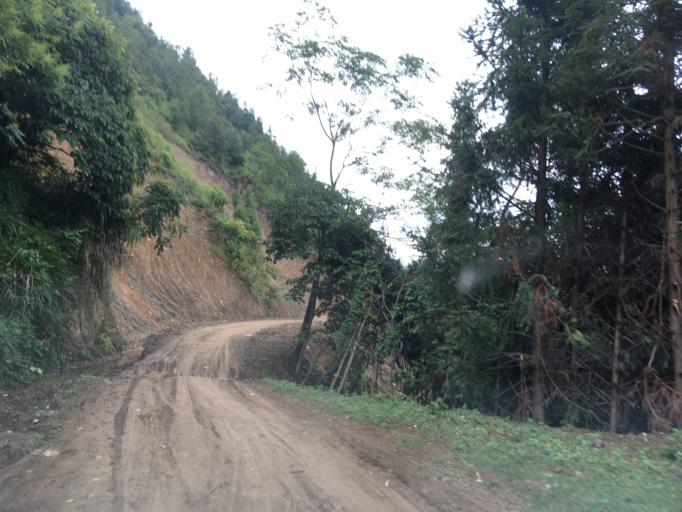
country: CN
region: Guangxi Zhuangzu Zizhiqu
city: Xinzhou
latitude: 24.8724
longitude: 105.8458
